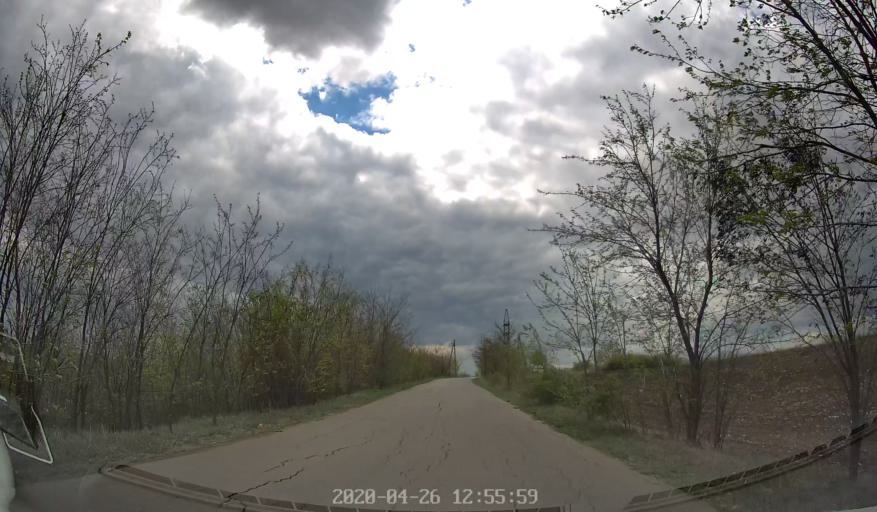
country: MD
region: Chisinau
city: Vadul lui Voda
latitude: 47.0753
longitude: 29.0661
